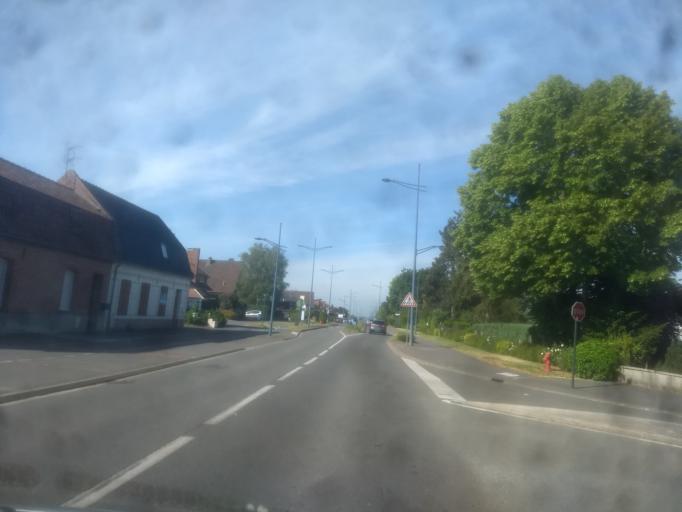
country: FR
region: Nord-Pas-de-Calais
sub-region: Departement du Pas-de-Calais
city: Dainville
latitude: 50.2784
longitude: 2.7284
